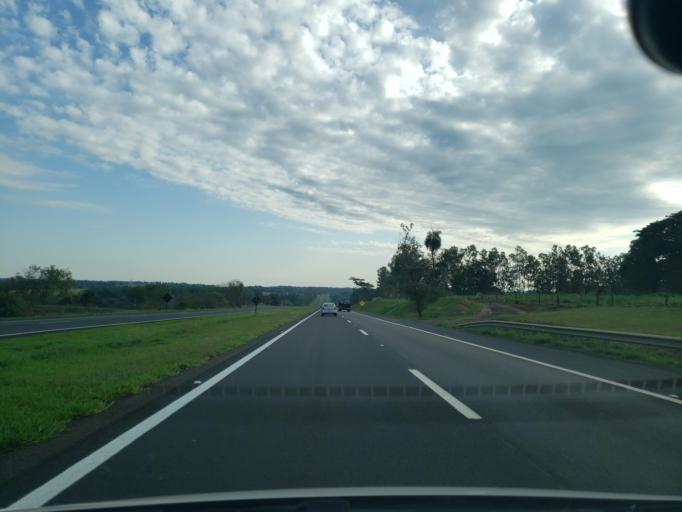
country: BR
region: Sao Paulo
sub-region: Guararapes
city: Guararapes
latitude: -21.2091
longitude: -50.6651
